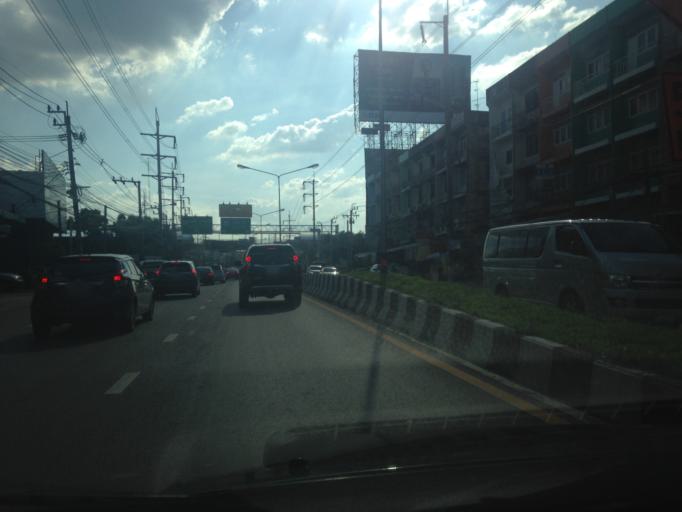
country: TH
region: Nonthaburi
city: Pak Kret
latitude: 13.9108
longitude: 100.5077
